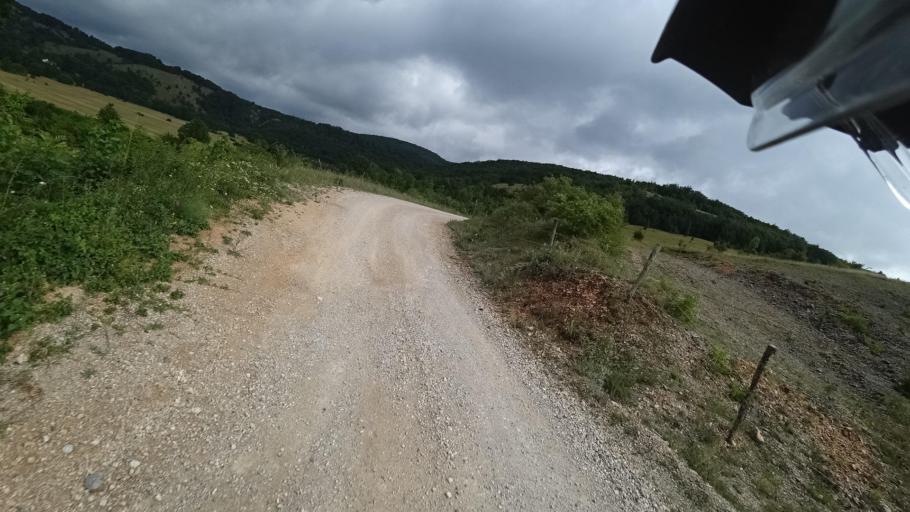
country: HR
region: Zadarska
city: Gracac
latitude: 44.5209
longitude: 15.8536
